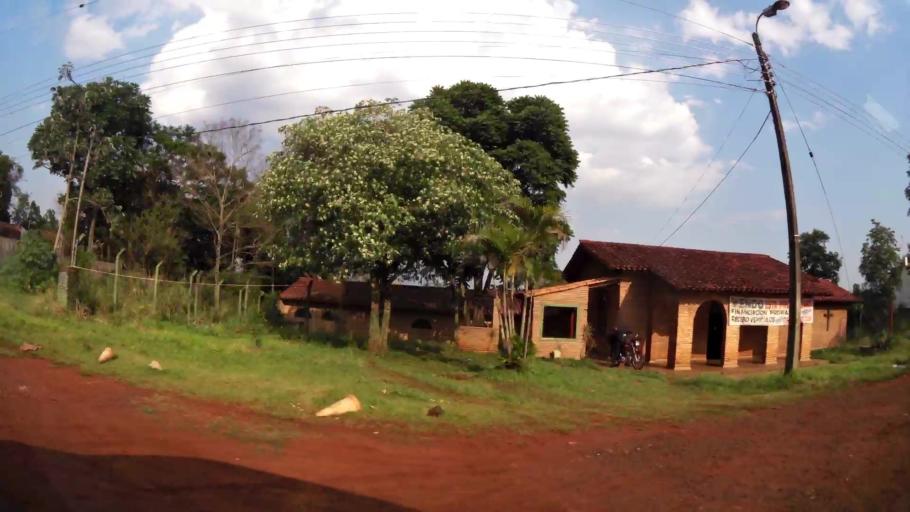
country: PY
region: Alto Parana
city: Presidente Franco
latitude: -25.5210
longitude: -54.6267
